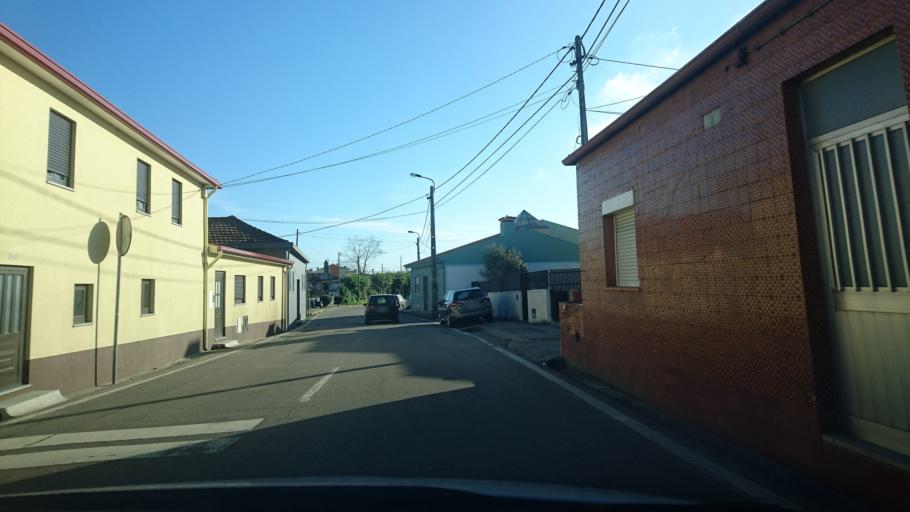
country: PT
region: Aveiro
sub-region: Espinho
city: Silvalde
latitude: 40.9883
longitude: -8.6305
